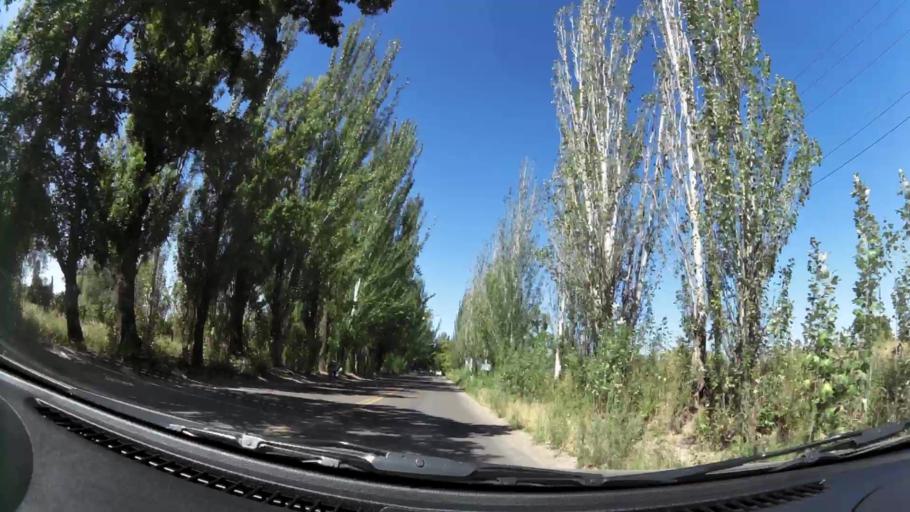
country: AR
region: Mendoza
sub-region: Departamento de Godoy Cruz
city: Godoy Cruz
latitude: -32.9855
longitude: -68.8450
